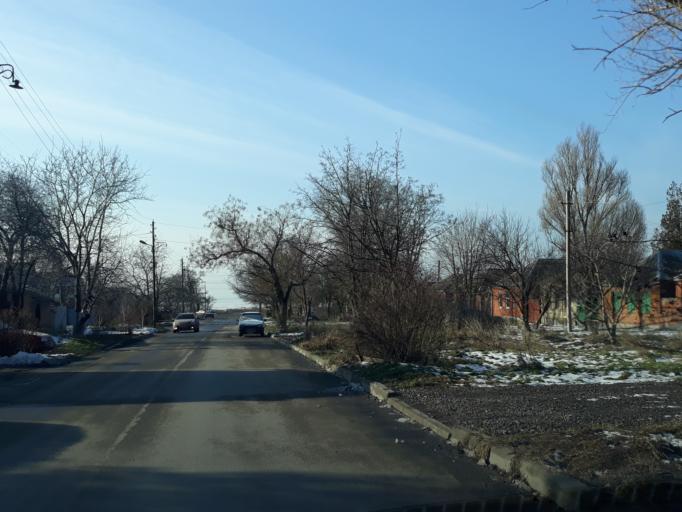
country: RU
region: Rostov
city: Taganrog
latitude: 47.2020
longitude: 38.9031
